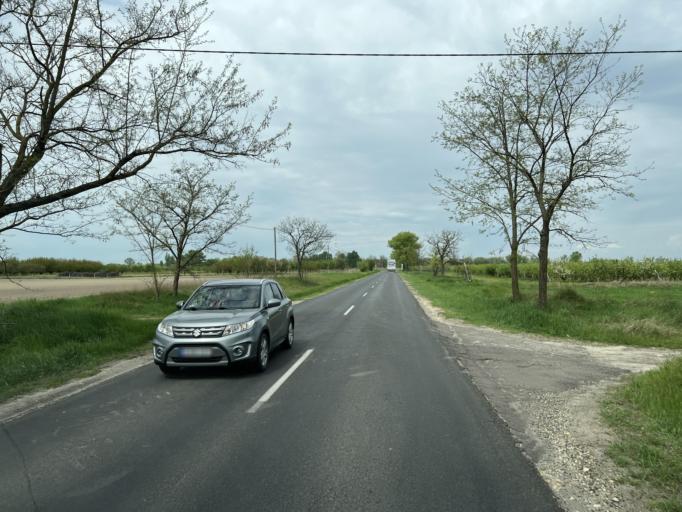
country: HU
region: Pest
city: Cegled
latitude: 47.1561
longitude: 19.8542
